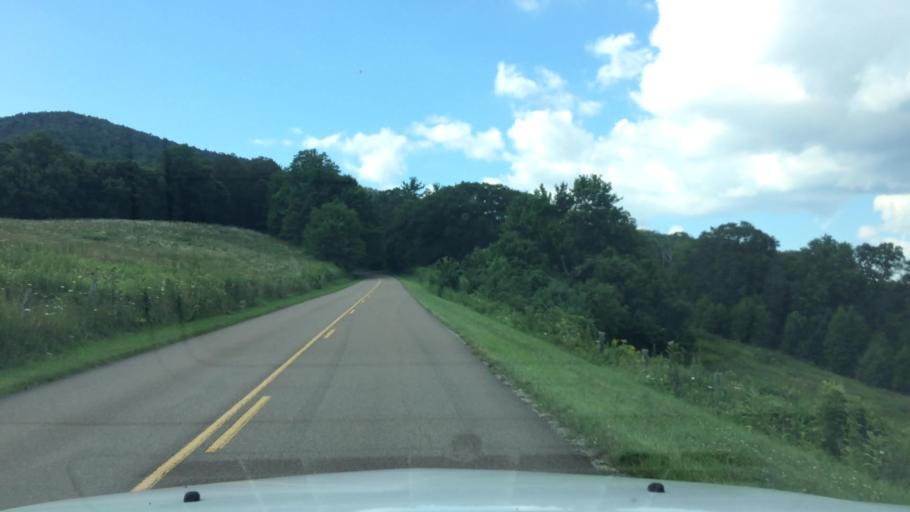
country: US
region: North Carolina
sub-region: Watauga County
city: Blowing Rock
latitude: 36.1520
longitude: -81.6667
